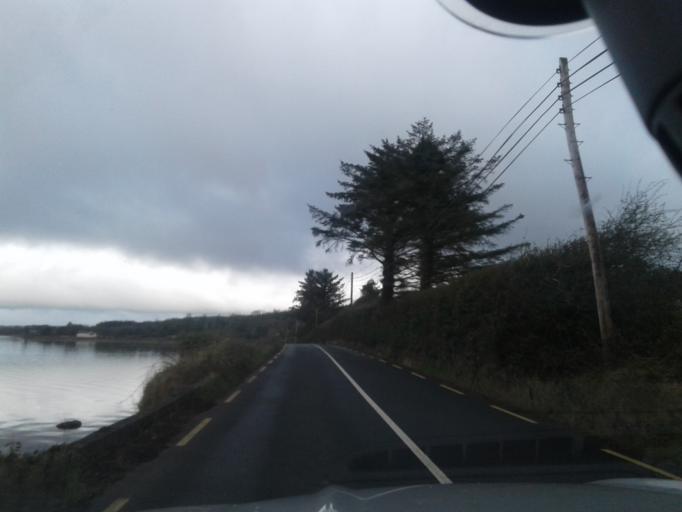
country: IE
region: Ulster
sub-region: County Donegal
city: Ramelton
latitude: 55.0869
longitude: -7.5662
